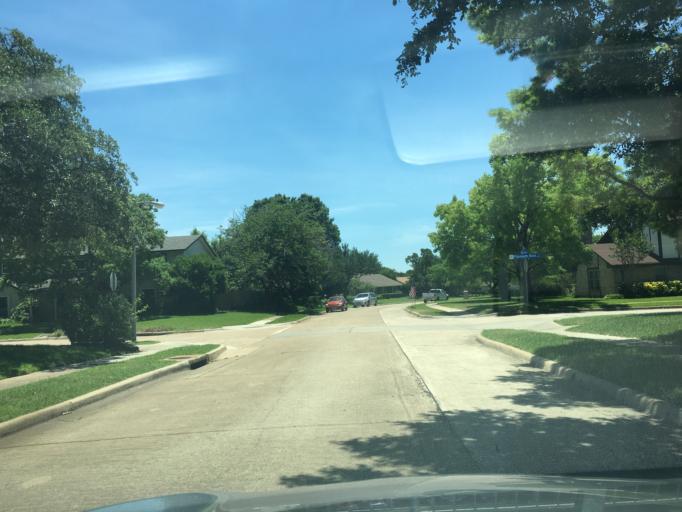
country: US
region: Texas
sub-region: Dallas County
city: Richardson
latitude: 32.9524
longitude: -96.6871
